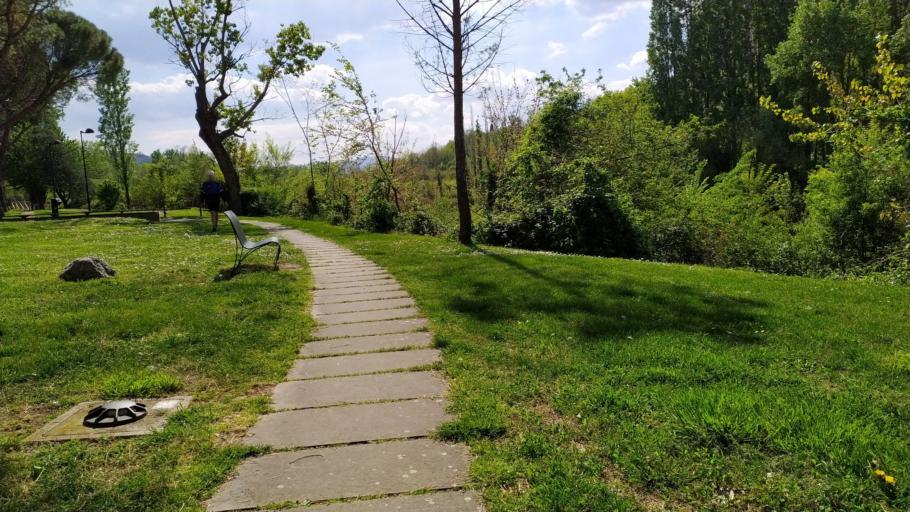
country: IT
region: Emilia-Romagna
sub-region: Provincia di Bologna
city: Borgo Tossignano
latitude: 44.2791
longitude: 11.5868
